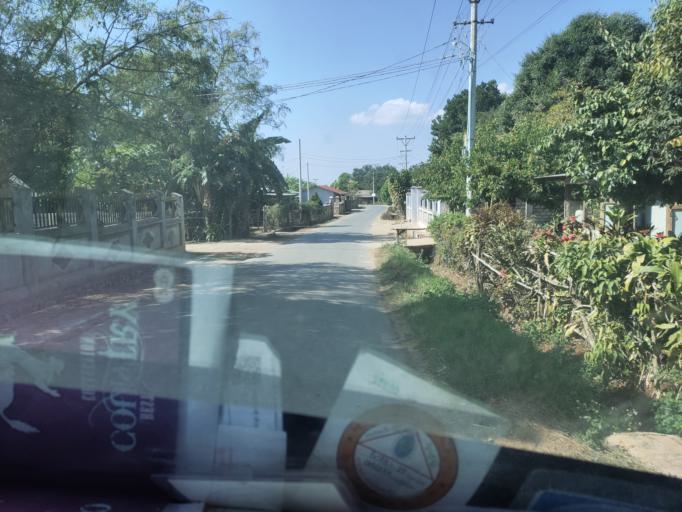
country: MM
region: Mandalay
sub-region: Pyin Oo Lwin District
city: Pyin Oo Lwin
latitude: 21.9537
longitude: 96.3914
